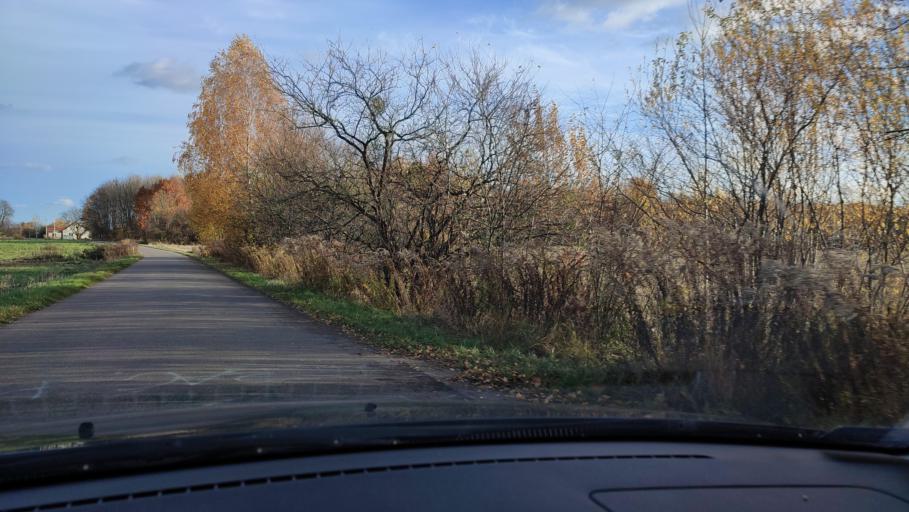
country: PL
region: Warmian-Masurian Voivodeship
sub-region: Powiat szczycienski
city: Szczytno
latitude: 53.5502
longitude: 20.9802
